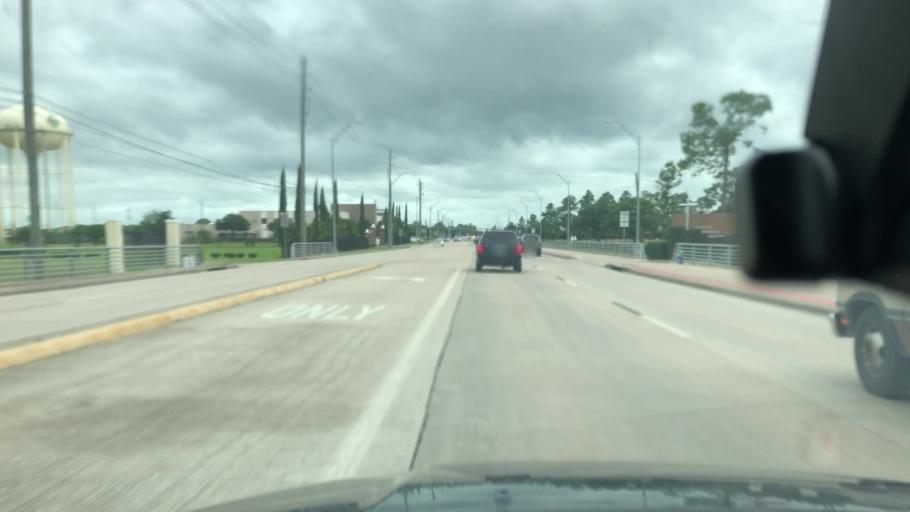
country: US
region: Texas
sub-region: Brazoria County
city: Brookside Village
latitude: 29.5656
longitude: -95.3506
